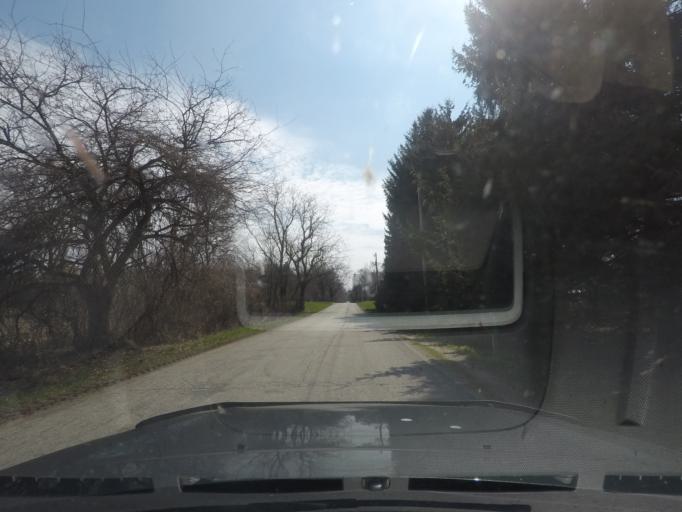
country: US
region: Indiana
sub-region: LaPorte County
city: Westville
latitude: 41.5236
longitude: -86.7989
